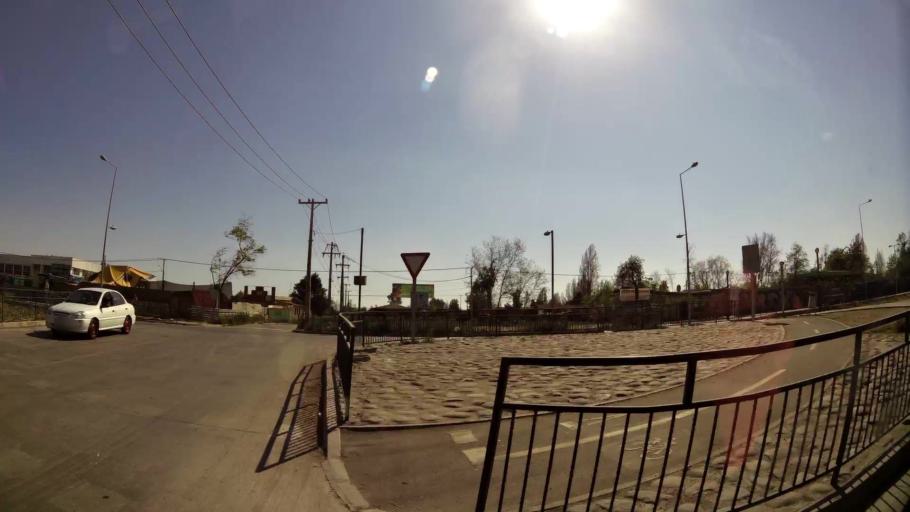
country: CL
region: Santiago Metropolitan
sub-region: Provincia de Santiago
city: La Pintana
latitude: -33.6209
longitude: -70.6271
